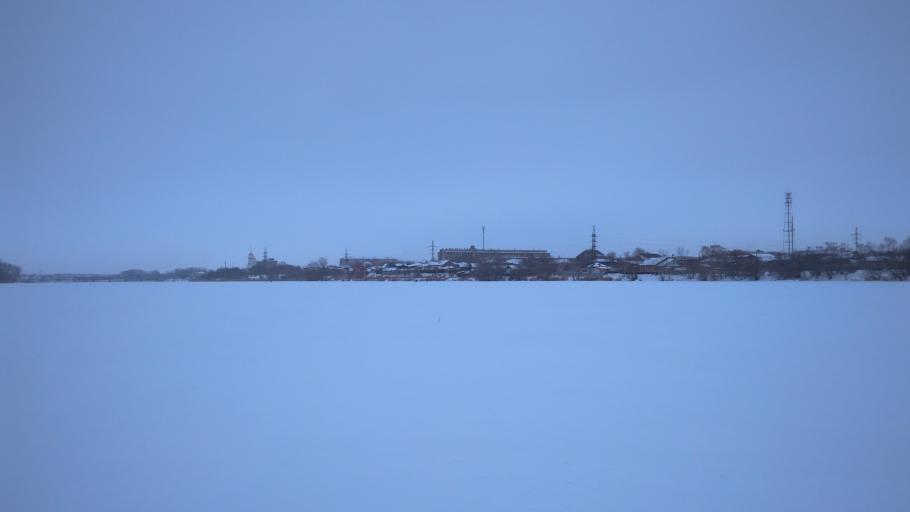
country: RU
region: Chelyabinsk
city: Troitsk
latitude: 54.0809
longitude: 61.5730
